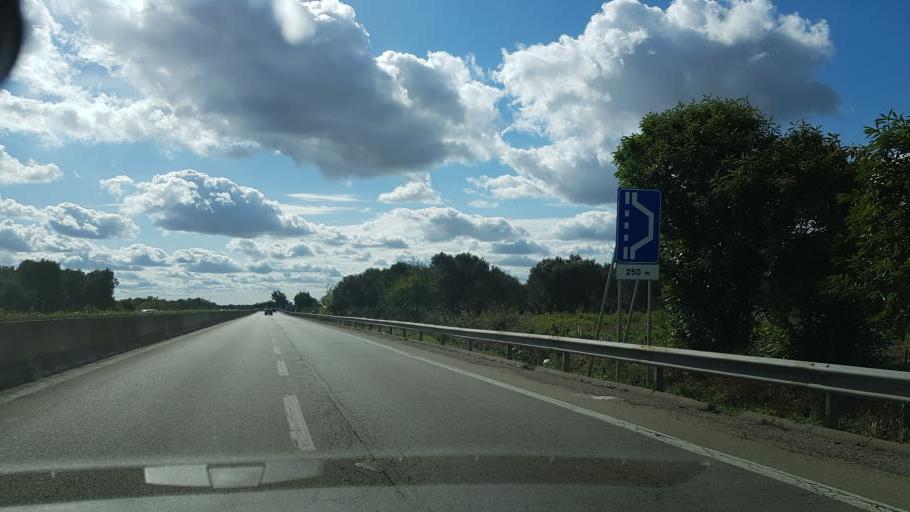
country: IT
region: Apulia
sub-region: Provincia di Brindisi
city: Tuturano
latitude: 40.5452
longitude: 17.9997
